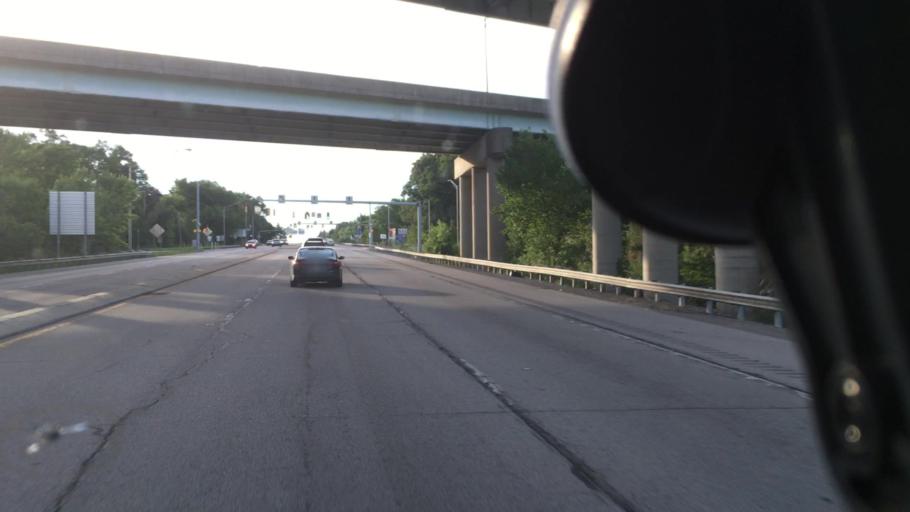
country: US
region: Pennsylvania
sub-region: Beaver County
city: West Mayfield
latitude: 40.7637
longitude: -80.3621
